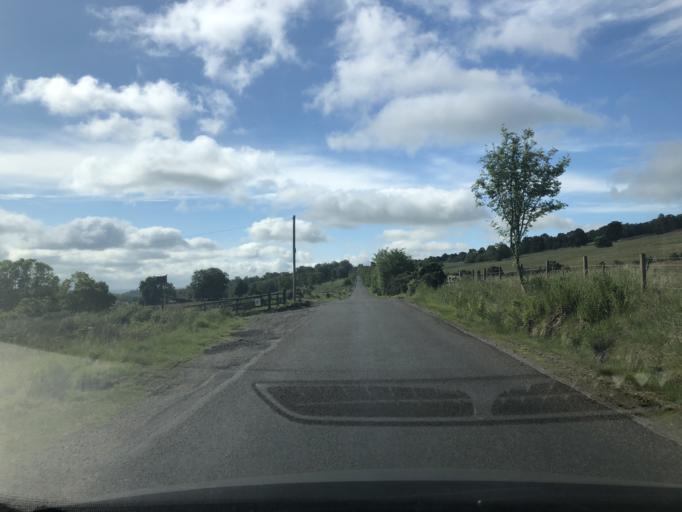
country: GB
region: Scotland
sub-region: Angus
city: Kirriemuir
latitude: 56.7526
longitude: -3.0154
